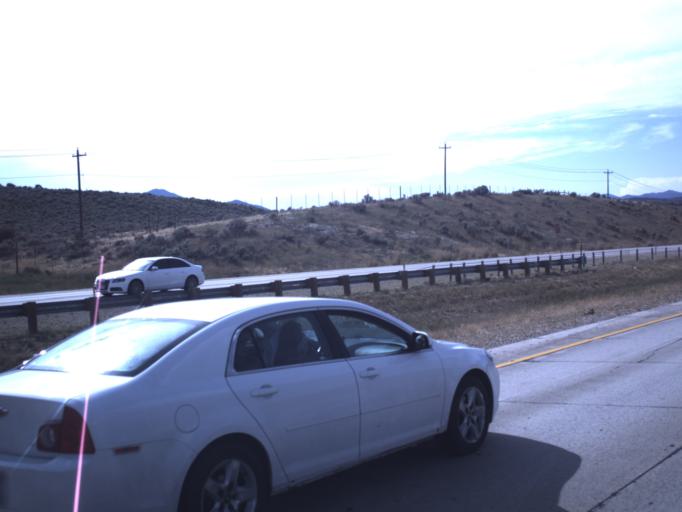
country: US
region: Utah
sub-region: Summit County
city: Park City
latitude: 40.7080
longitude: -111.4792
